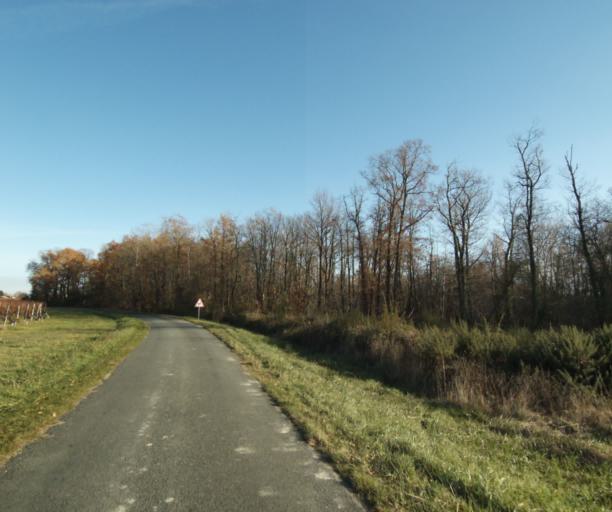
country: FR
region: Poitou-Charentes
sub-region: Departement de la Charente-Maritime
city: Burie
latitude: 45.7765
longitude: -0.4477
